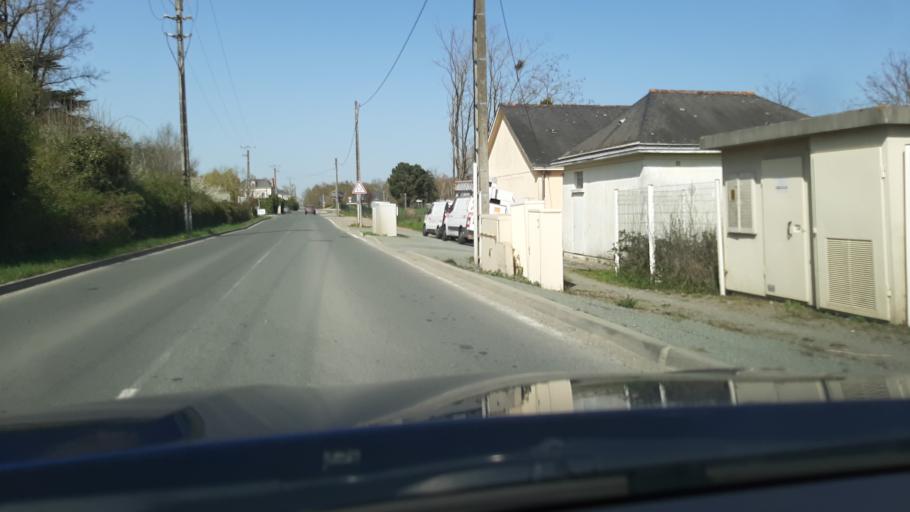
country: FR
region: Pays de la Loire
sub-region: Departement de Maine-et-Loire
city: Pellouailles-les-Vignes
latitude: 47.5145
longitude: -0.4556
